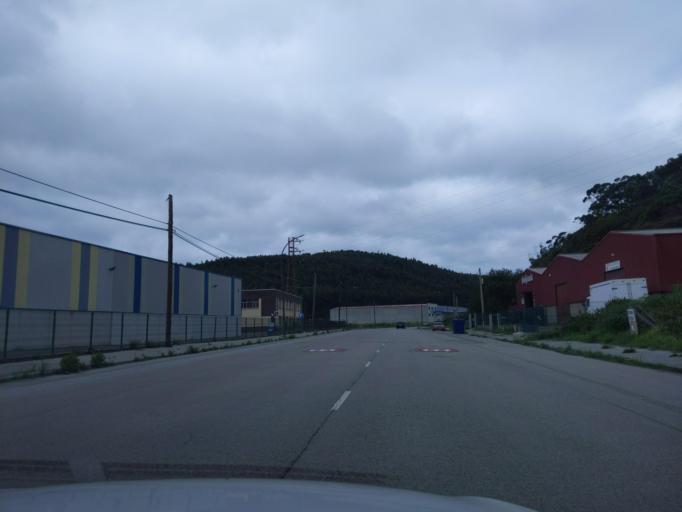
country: ES
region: Asturias
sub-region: Province of Asturias
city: Aviles
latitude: 43.5966
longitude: -5.9141
